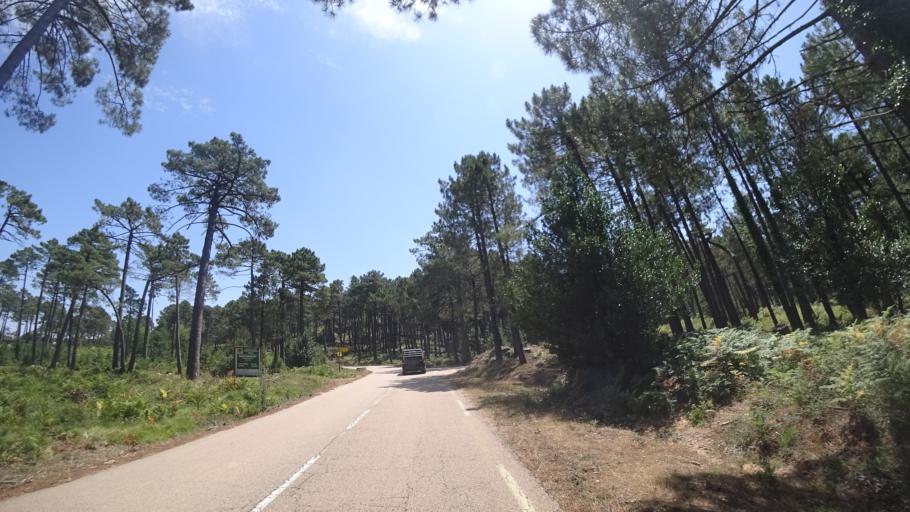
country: FR
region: Corsica
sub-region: Departement de la Corse-du-Sud
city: Zonza
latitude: 41.6860
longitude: 9.1958
